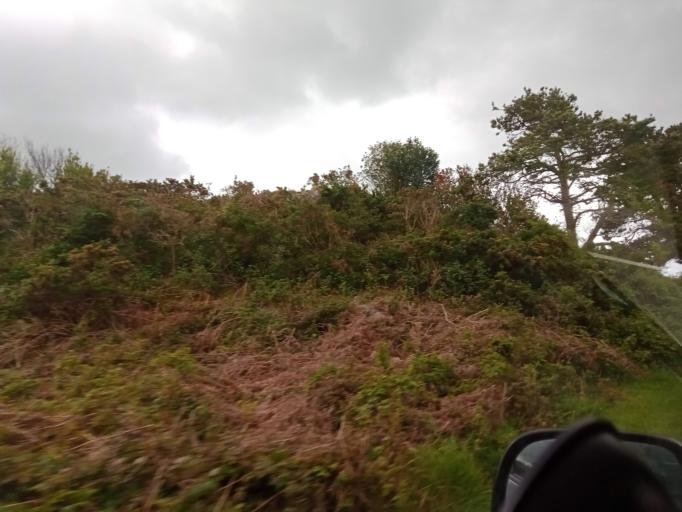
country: IE
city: Farranacoush
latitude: 51.5055
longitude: -9.3518
